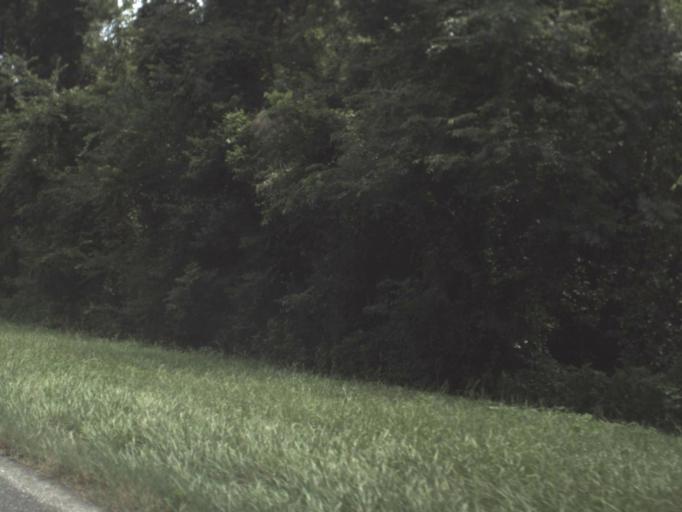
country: US
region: Florida
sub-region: Alachua County
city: High Springs
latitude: 29.9834
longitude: -82.5978
